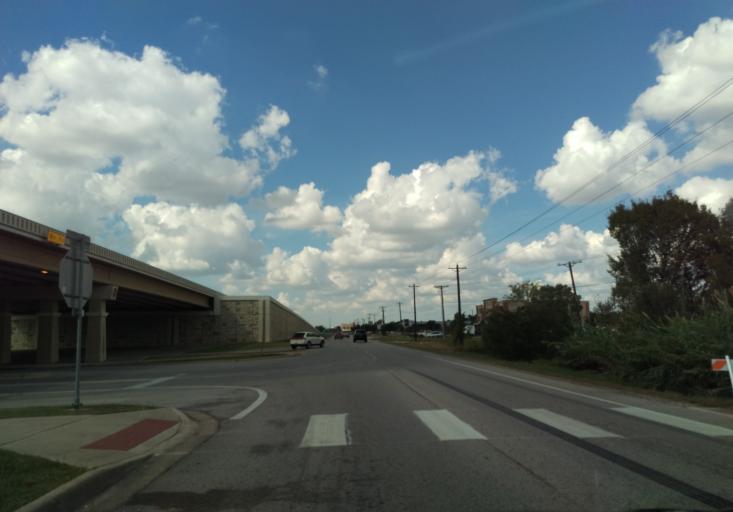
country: US
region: Texas
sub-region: Brazos County
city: College Station
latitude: 30.5722
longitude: -96.2738
